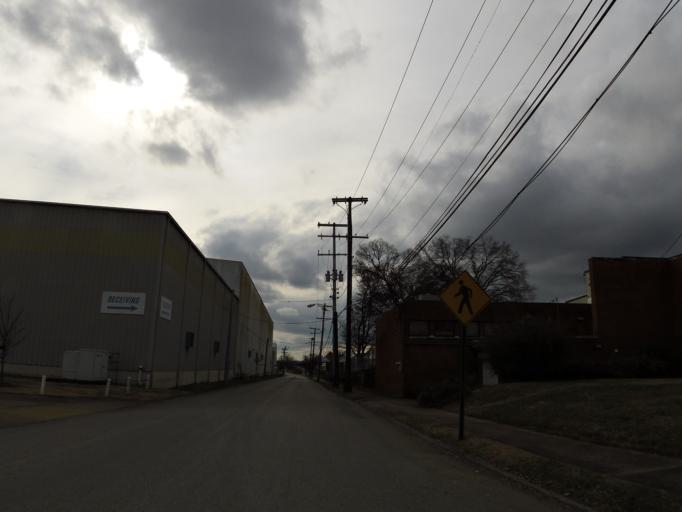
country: US
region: Tennessee
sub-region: Hamilton County
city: Chattanooga
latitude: 35.0308
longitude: -85.2934
